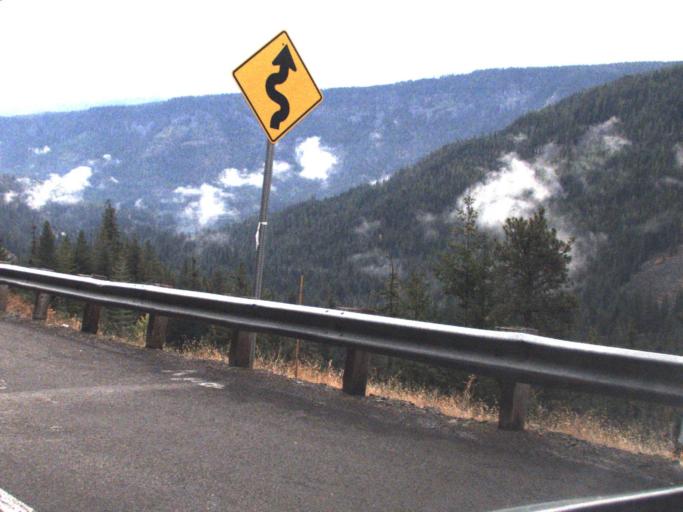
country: US
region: Washington
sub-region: Yakima County
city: Tieton
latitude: 46.6550
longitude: -121.3040
